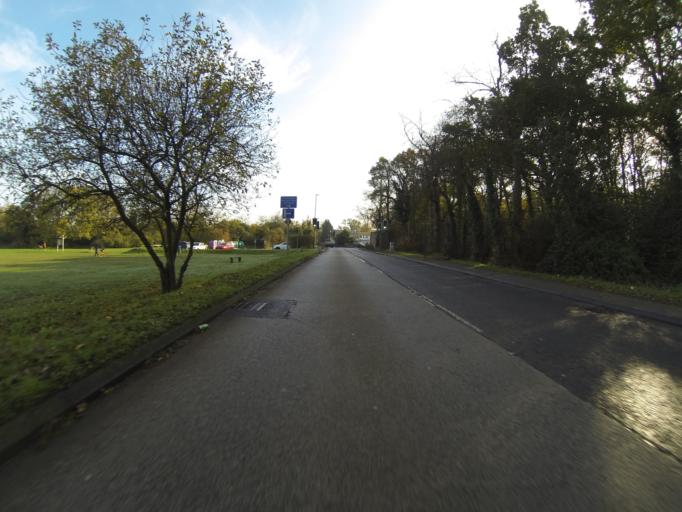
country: GB
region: England
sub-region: Kent
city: Dartford
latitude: 51.4313
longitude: 0.1950
